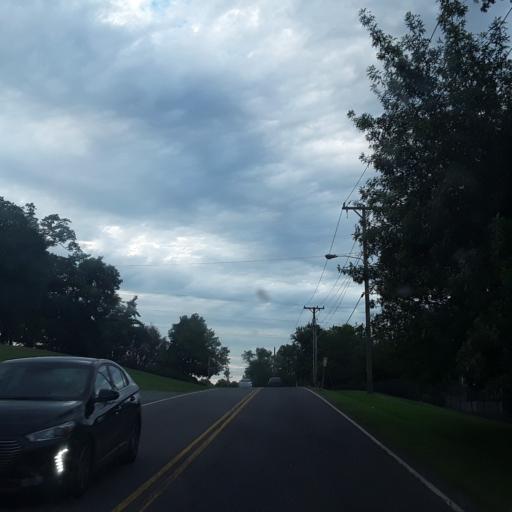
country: US
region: Tennessee
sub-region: Wilson County
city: Green Hill
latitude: 36.1624
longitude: -86.5972
